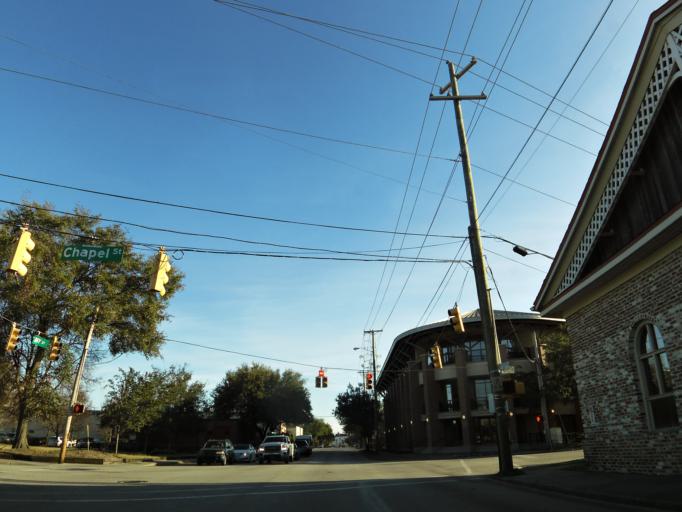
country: US
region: South Carolina
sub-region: Charleston County
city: Charleston
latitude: 32.7922
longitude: -79.9312
